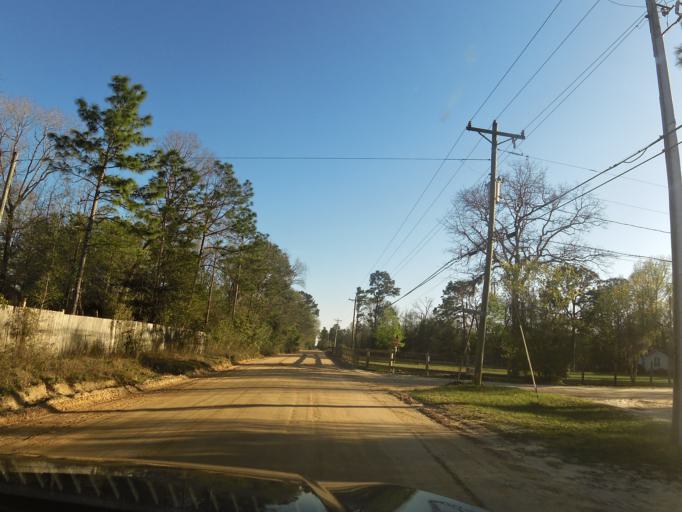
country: US
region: Florida
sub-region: Clay County
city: Middleburg
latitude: 30.1332
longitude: -81.8819
